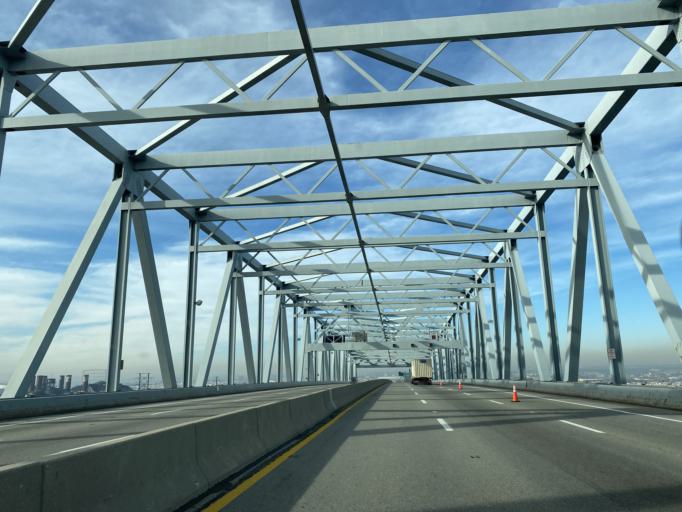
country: US
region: New Jersey
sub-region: Camden County
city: Pennsauken
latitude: 39.9850
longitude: -75.0665
